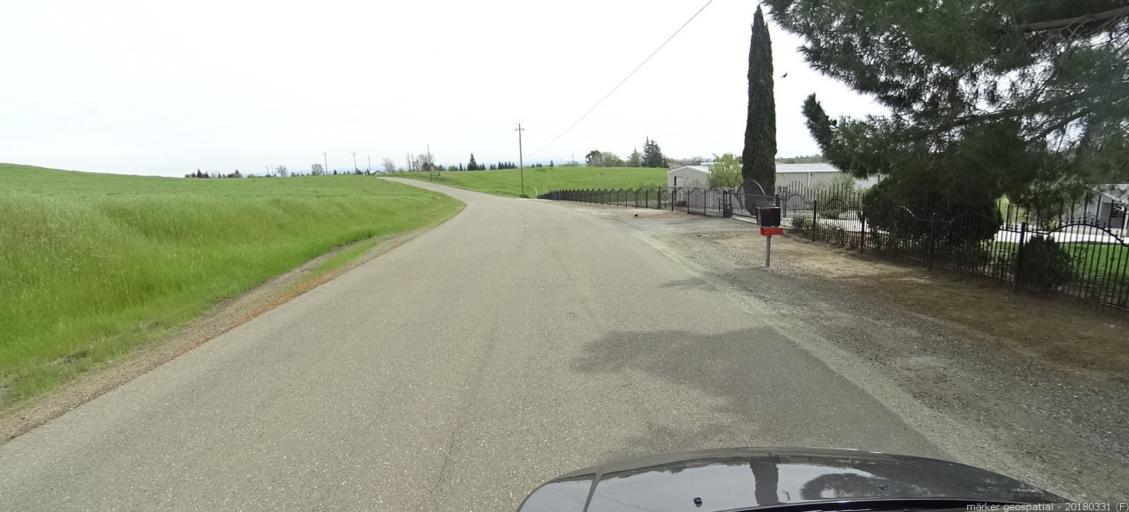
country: US
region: California
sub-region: Sacramento County
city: Rancho Murieta
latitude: 38.4893
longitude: -121.1379
